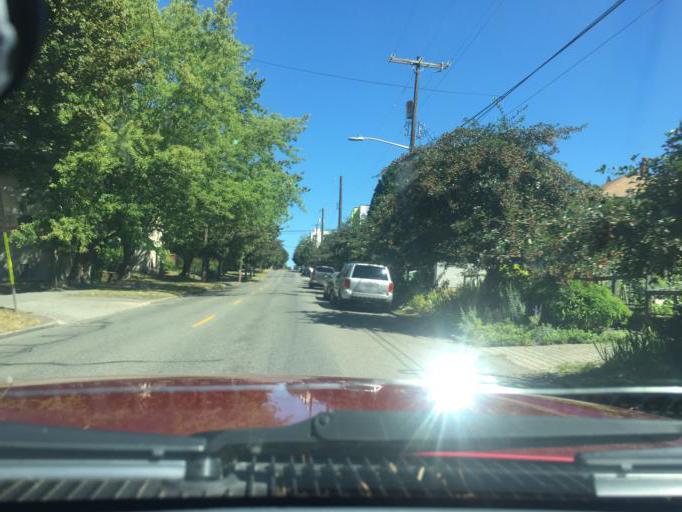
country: US
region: Washington
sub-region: King County
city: Seattle
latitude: 47.6028
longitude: -122.3142
